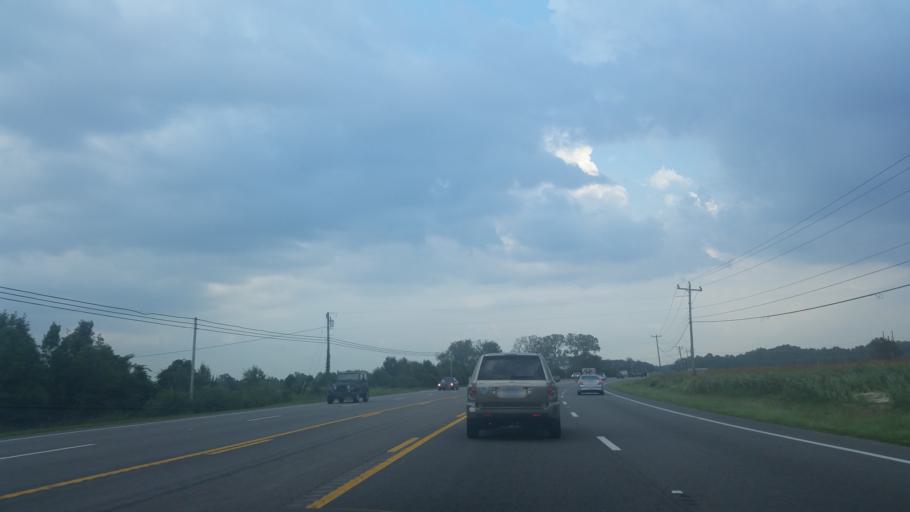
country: US
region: North Carolina
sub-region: Dare County
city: Southern Shores
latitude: 36.1963
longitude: -75.8640
